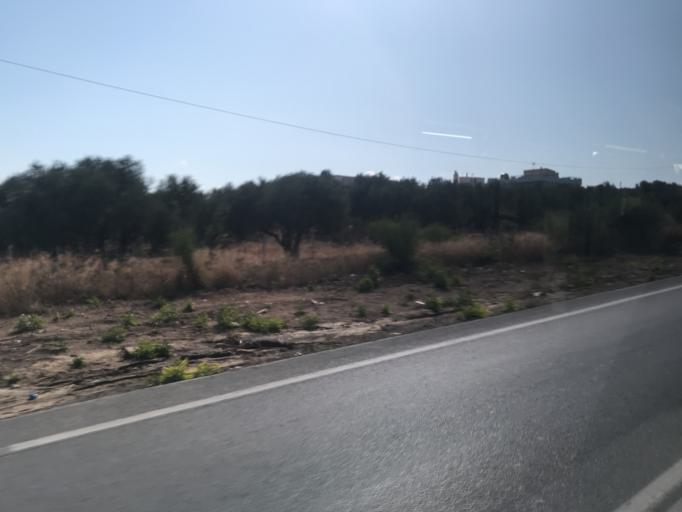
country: GR
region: Crete
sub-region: Nomos Irakleiou
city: Gazi
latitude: 35.3128
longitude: 25.0915
